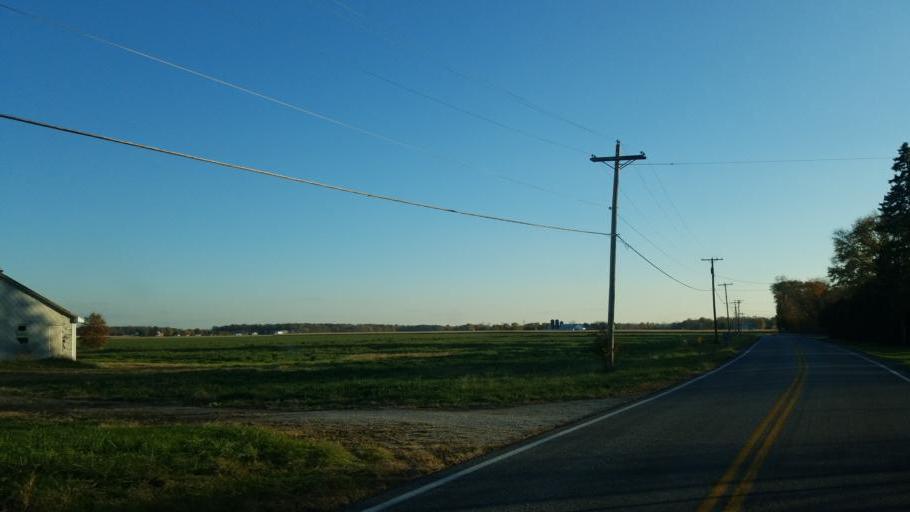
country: US
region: Ohio
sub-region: Sandusky County
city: Green Springs
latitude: 41.3213
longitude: -83.0566
